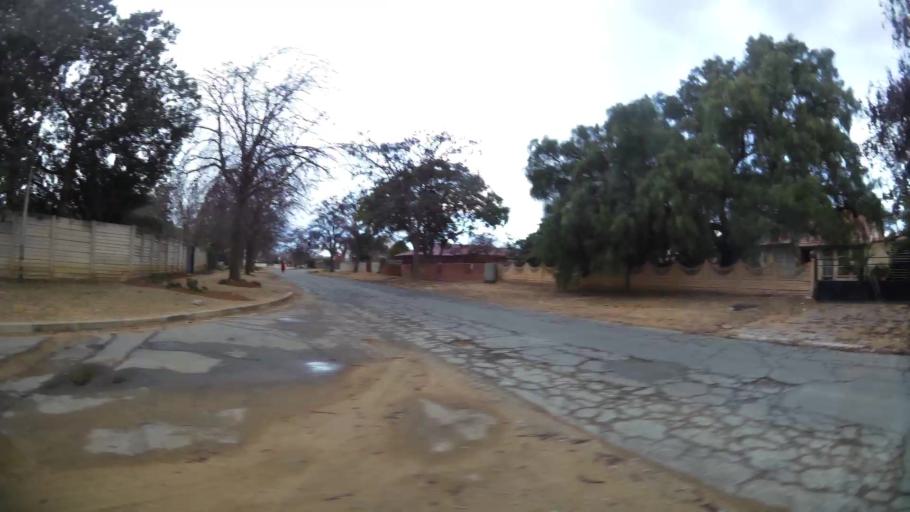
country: ZA
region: Orange Free State
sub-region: Lejweleputswa District Municipality
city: Welkom
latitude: -27.9675
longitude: 26.7245
